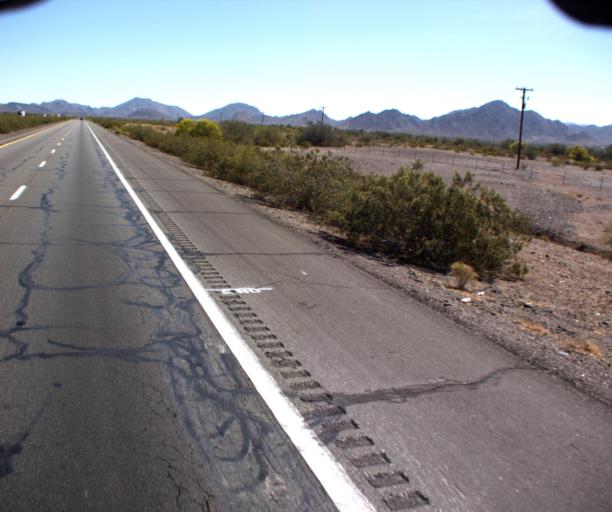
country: US
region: Arizona
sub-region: La Paz County
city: Quartzsite
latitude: 33.6707
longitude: -114.1553
